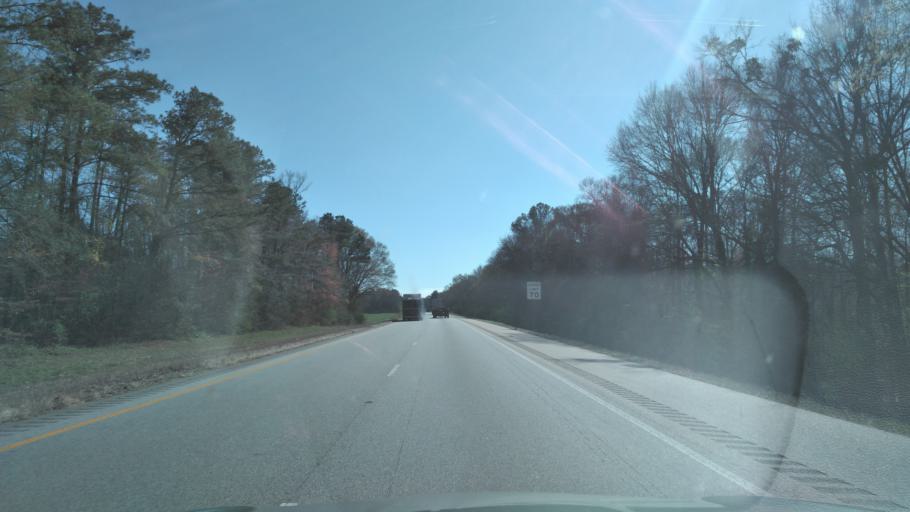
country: US
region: Alabama
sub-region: Lowndes County
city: Fort Deposit
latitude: 31.9777
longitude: -86.5334
